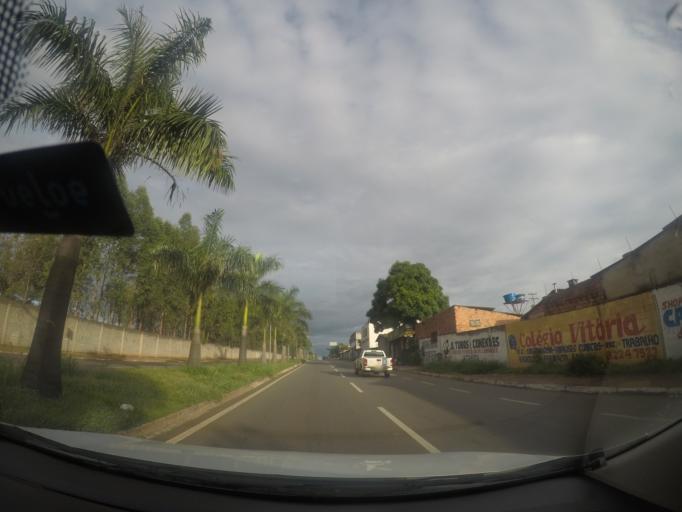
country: BR
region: Goias
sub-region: Goiania
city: Goiania
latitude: -16.6345
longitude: -49.3218
